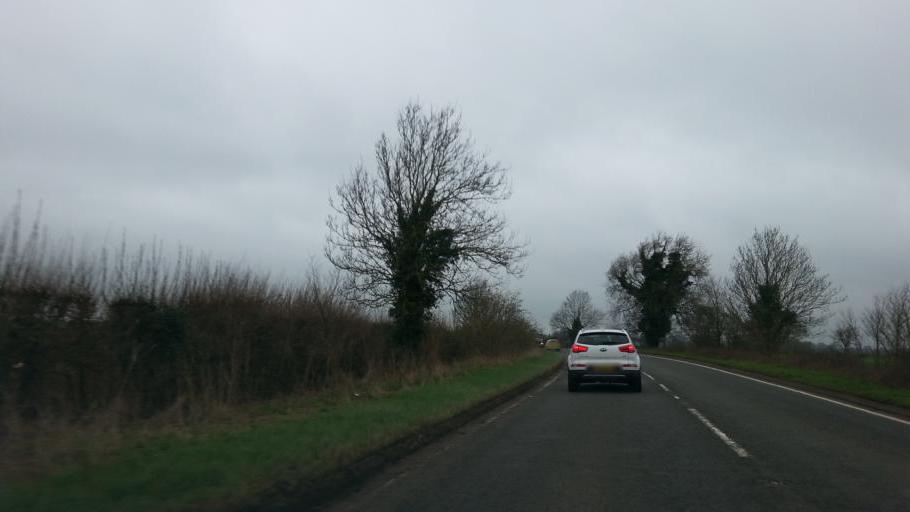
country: GB
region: England
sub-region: Oxfordshire
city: Adderbury
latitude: 52.0633
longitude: -1.2487
